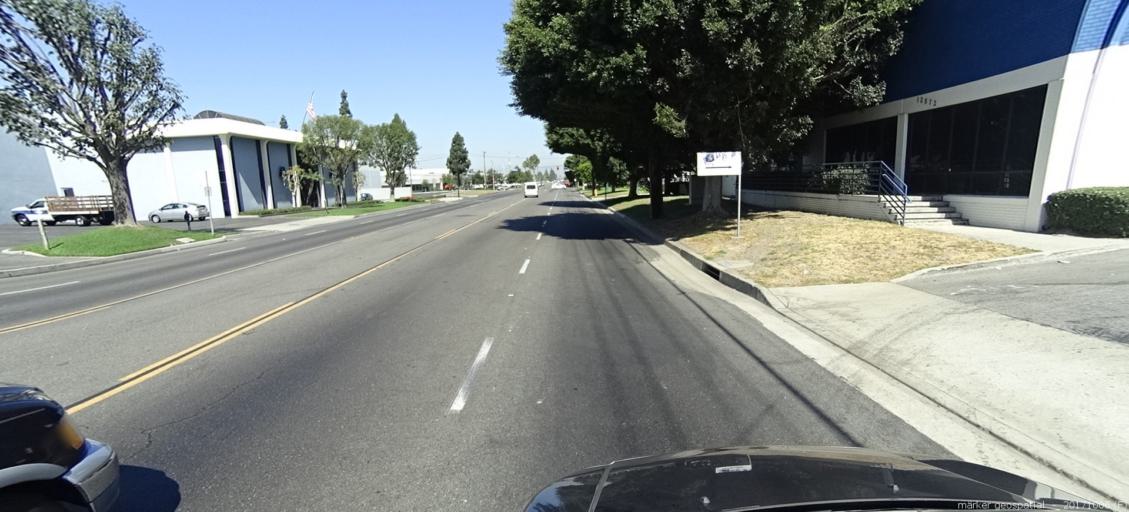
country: US
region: California
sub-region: Orange County
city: Westminster
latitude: 33.7792
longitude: -118.0014
